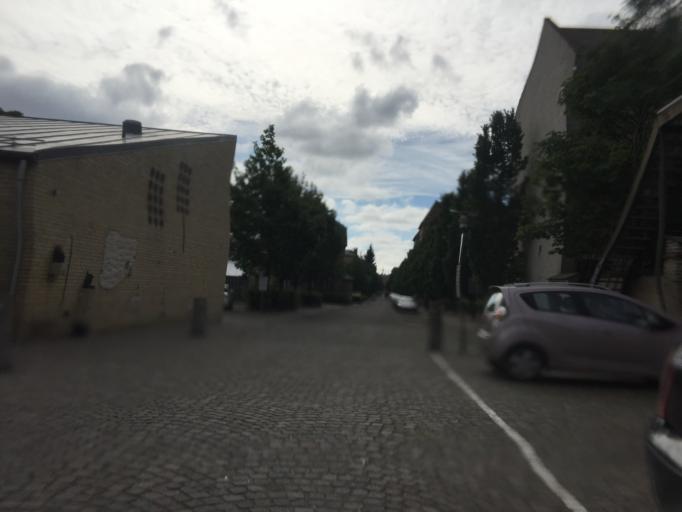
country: DK
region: Capital Region
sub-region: Frederiksberg Kommune
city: Frederiksberg
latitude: 55.6793
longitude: 12.5389
